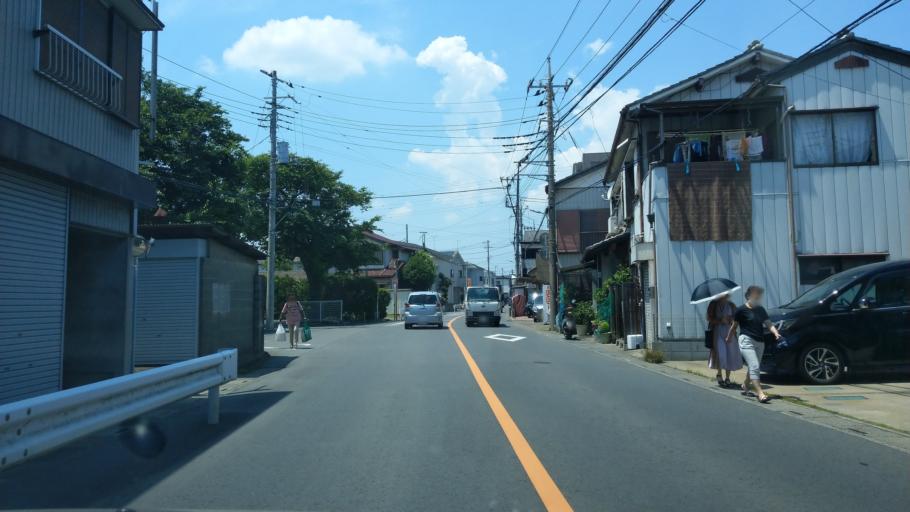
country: JP
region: Saitama
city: Shimotoda
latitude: 35.8627
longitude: 139.6850
